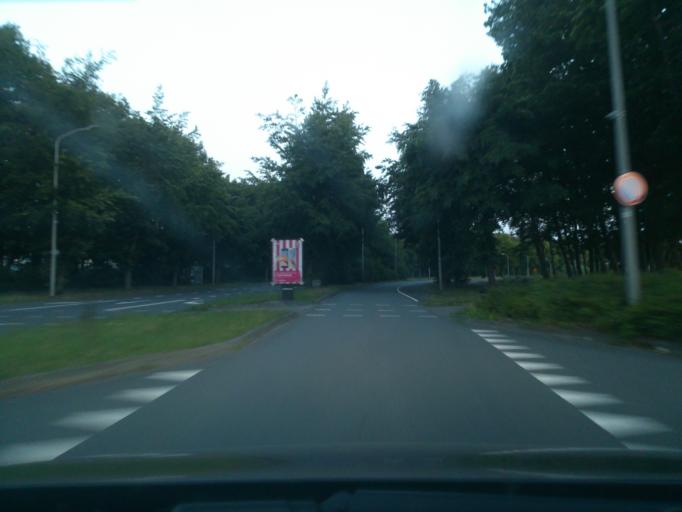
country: NL
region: Gelderland
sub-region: Gemeente Nijmegen
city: Nijmegen
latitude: 51.8192
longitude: 5.8285
